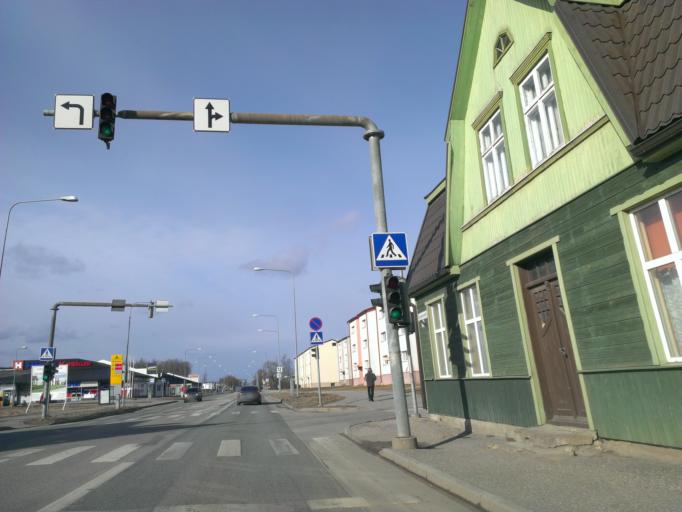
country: EE
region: Paernumaa
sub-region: Paernu linn
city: Parnu
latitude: 58.4025
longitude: 24.4929
